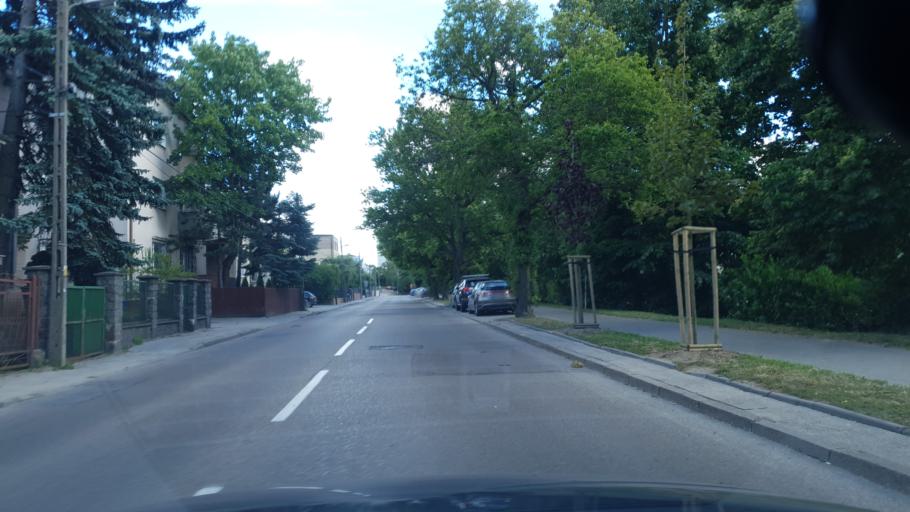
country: PL
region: Pomeranian Voivodeship
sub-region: Gdynia
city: Gdynia
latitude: 54.5011
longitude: 18.5412
